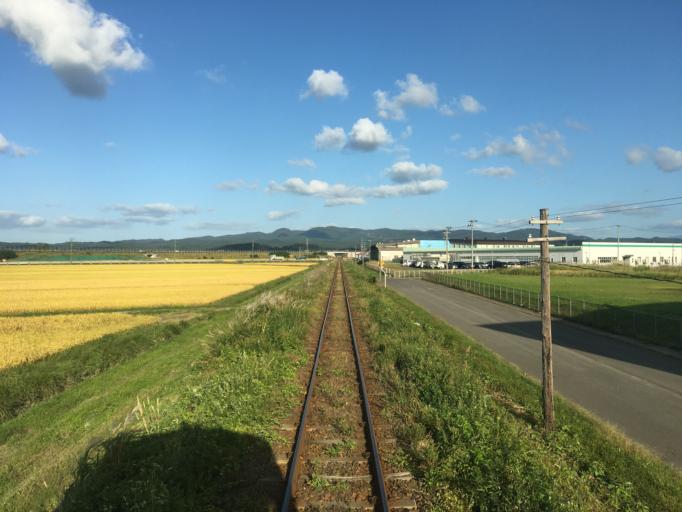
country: JP
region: Aomori
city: Goshogawara
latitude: 40.8182
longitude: 140.4634
